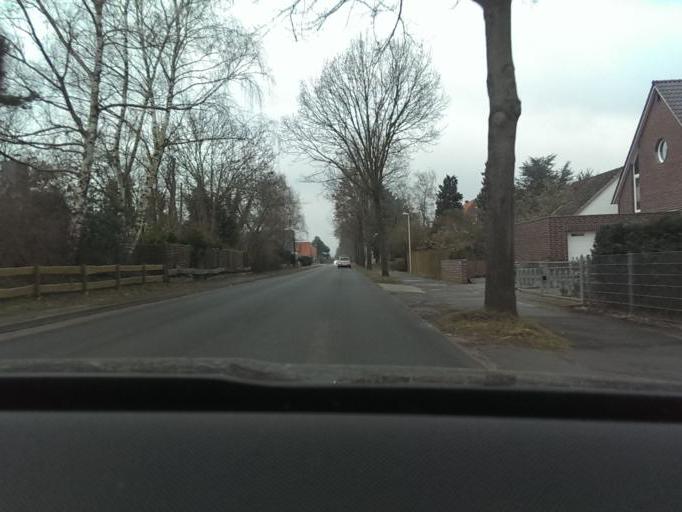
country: DE
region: Lower Saxony
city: Isernhagen Farster Bauerschaft
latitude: 52.4599
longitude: 9.8257
